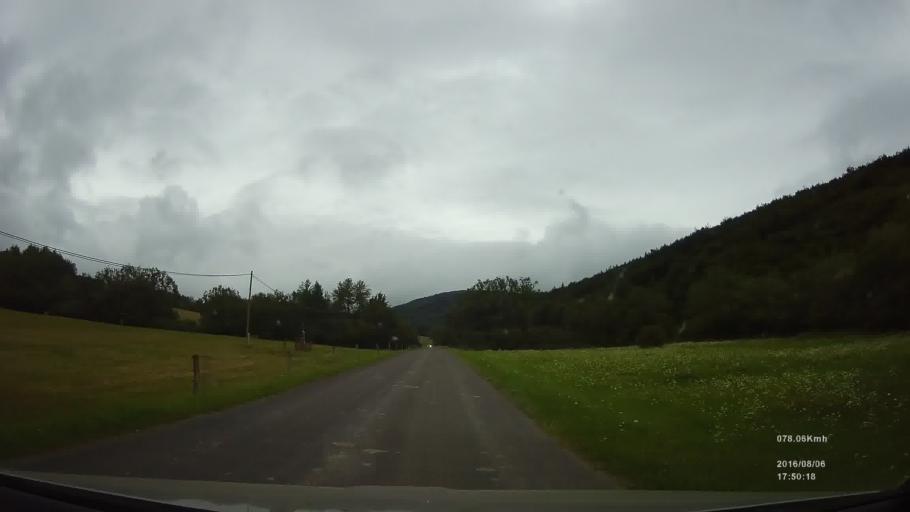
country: SK
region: Presovsky
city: Svidnik
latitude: 49.3906
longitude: 21.5666
